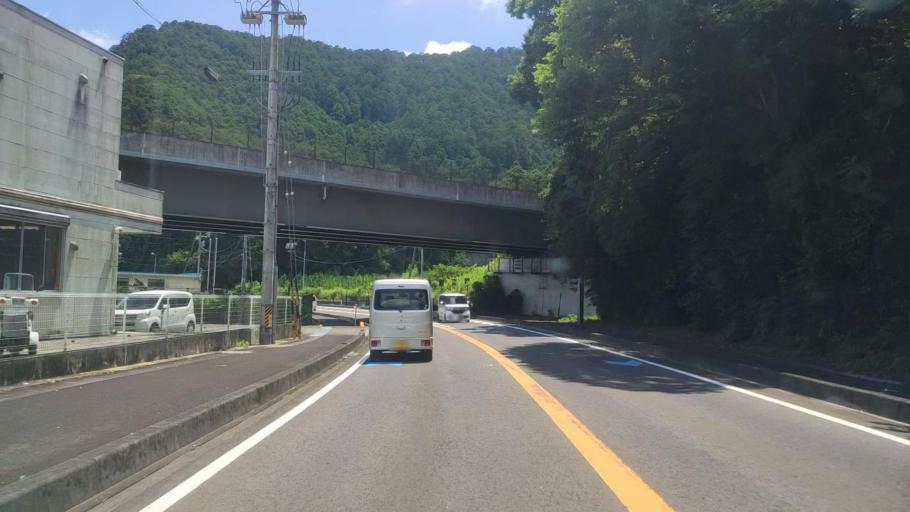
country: JP
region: Mie
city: Owase
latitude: 34.1162
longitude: 136.2196
